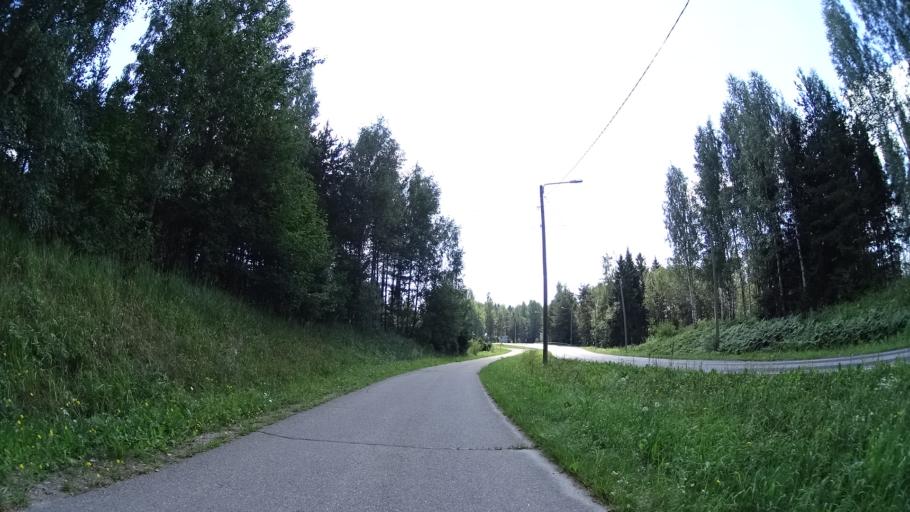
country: FI
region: Uusimaa
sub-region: Helsinki
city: Tuusula
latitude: 60.3487
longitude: 25.0034
